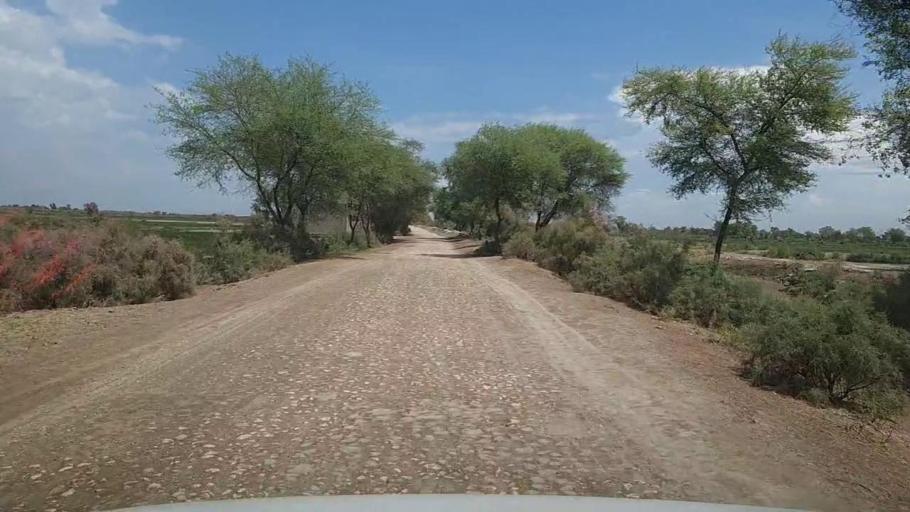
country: PK
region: Sindh
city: Kandhkot
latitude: 28.3405
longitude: 69.2448
